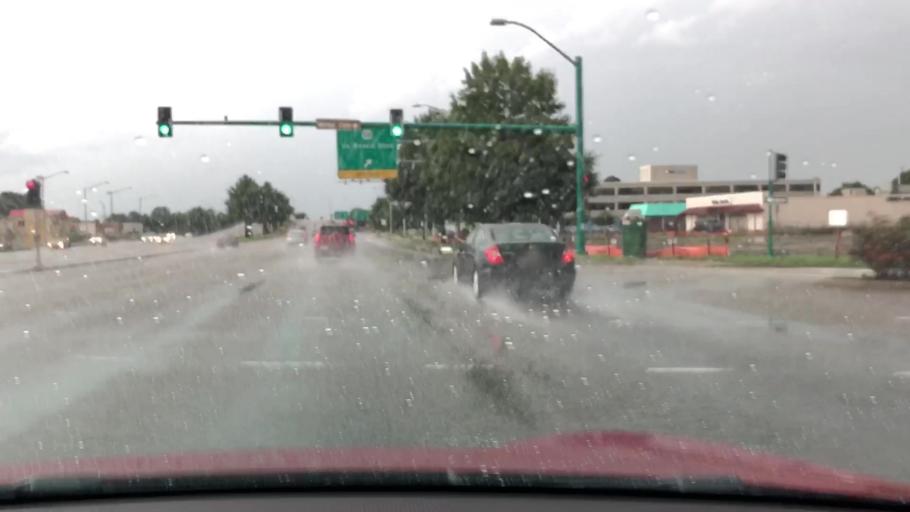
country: US
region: Virginia
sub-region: City of Chesapeake
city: Chesapeake
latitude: 36.8517
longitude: -76.2099
